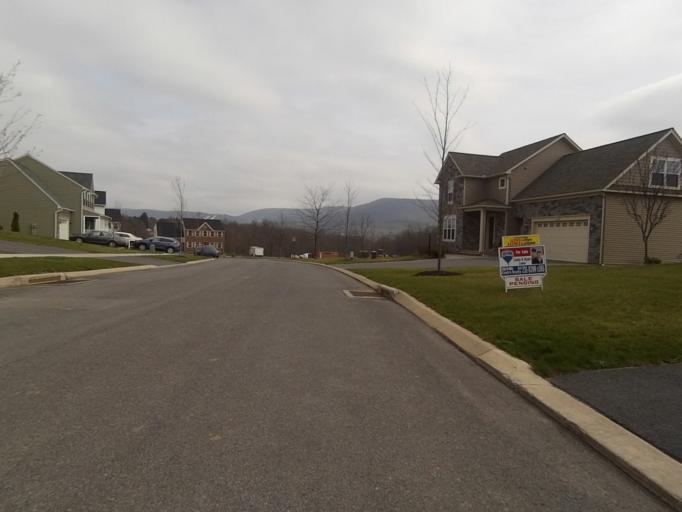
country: US
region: Pennsylvania
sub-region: Centre County
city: Boalsburg
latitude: 40.7875
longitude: -77.8030
